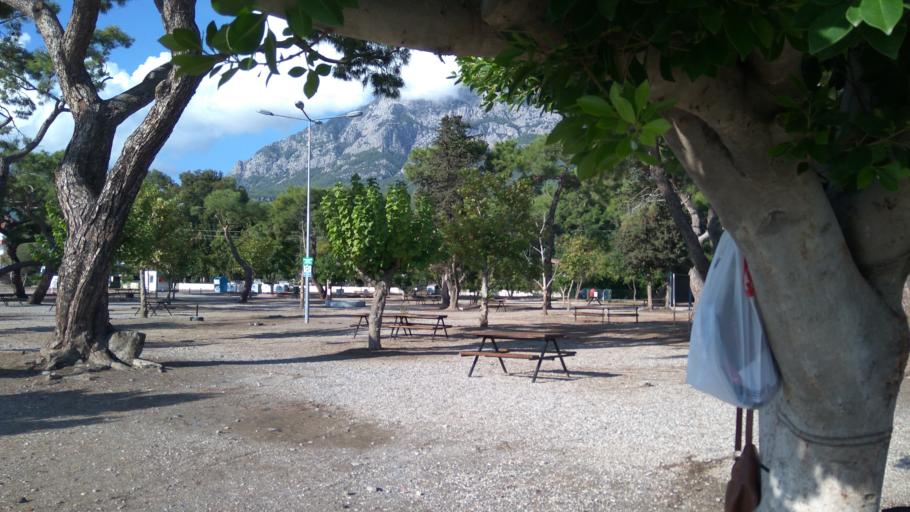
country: TR
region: Antalya
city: Kemer
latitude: 36.6257
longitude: 30.5563
